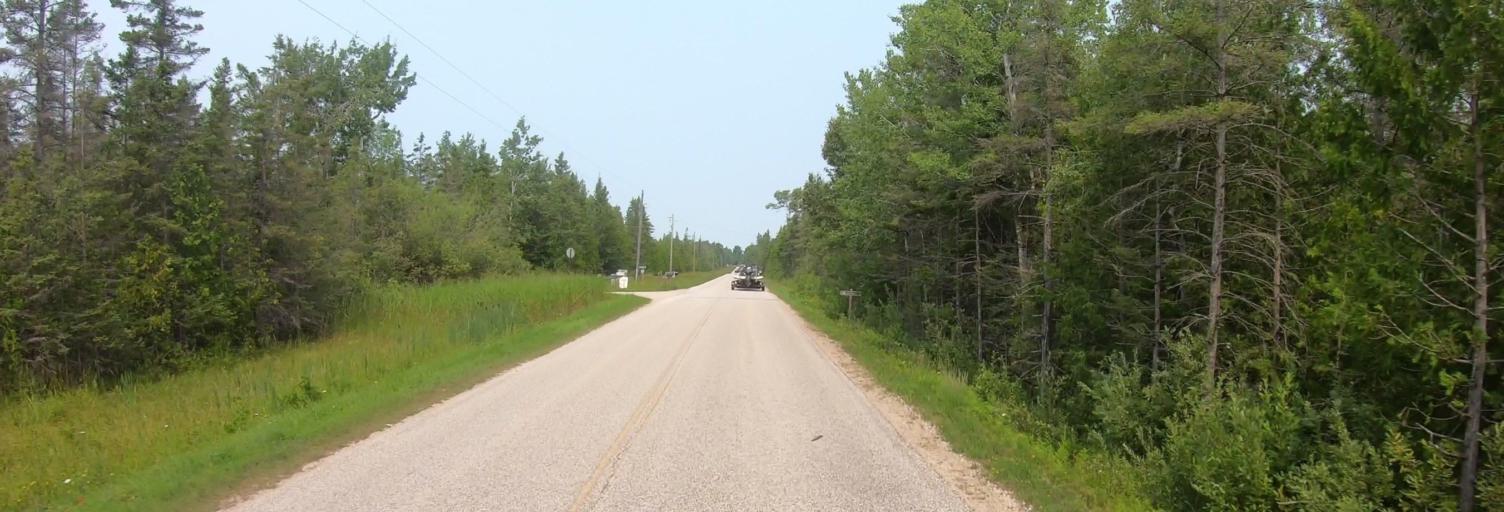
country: CA
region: Ontario
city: Thessalon
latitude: 46.0449
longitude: -83.6662
